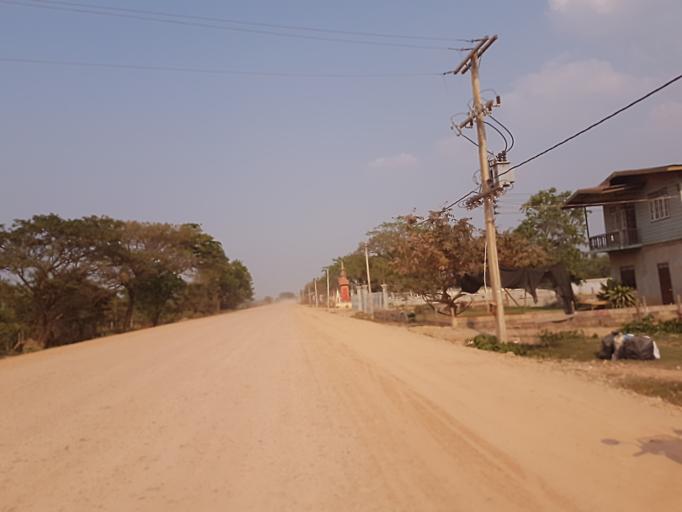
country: TH
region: Nong Khai
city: Phon Phisai
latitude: 17.9856
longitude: 102.8952
